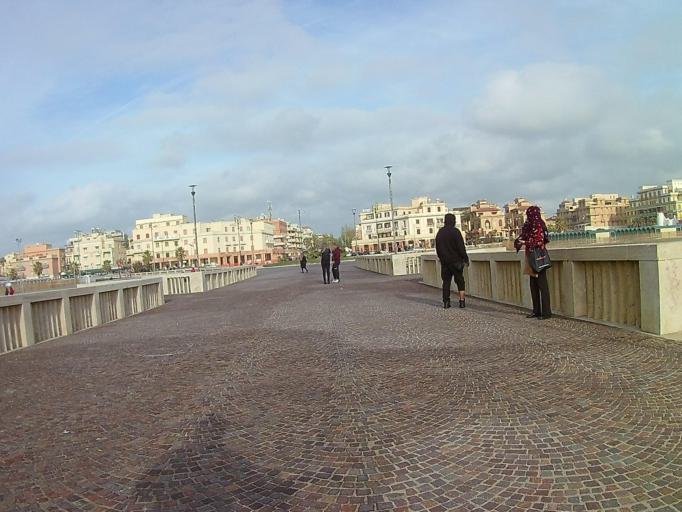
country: IT
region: Latium
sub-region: Citta metropolitana di Roma Capitale
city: Lido di Ostia
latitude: 41.7285
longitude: 12.2757
